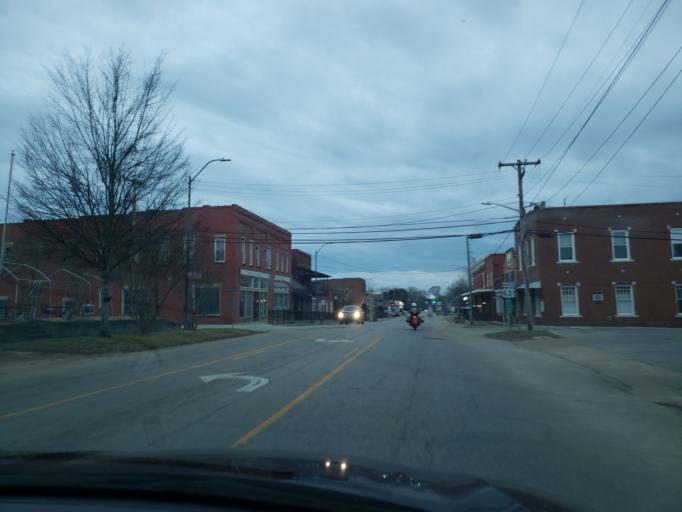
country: US
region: Alabama
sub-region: Chambers County
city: Lafayette
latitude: 32.8980
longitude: -85.4012
